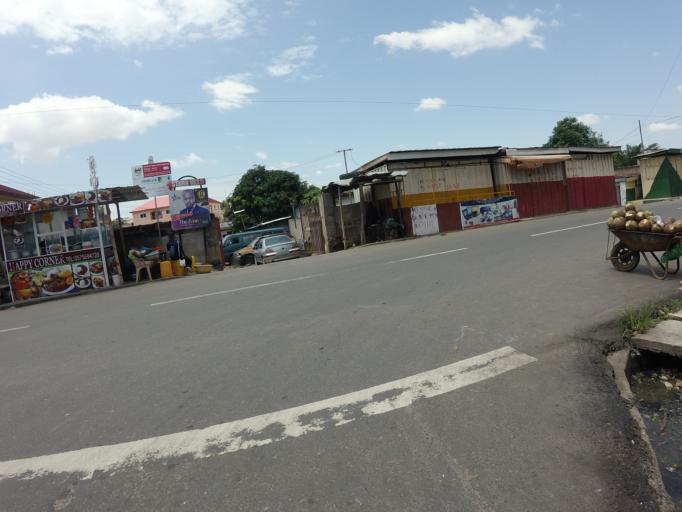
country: GH
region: Greater Accra
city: Accra
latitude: 5.5773
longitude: -0.2033
